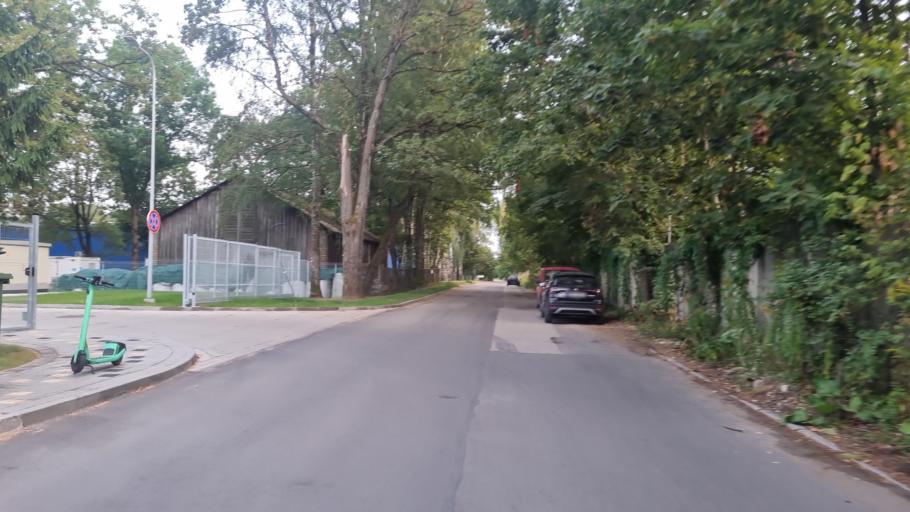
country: LV
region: Kekava
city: Balozi
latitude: 56.9087
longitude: 24.1519
